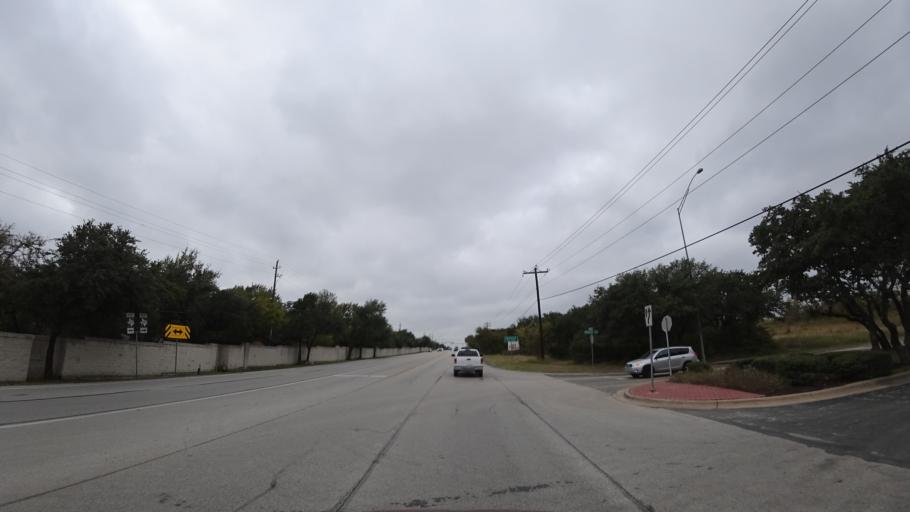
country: US
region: Texas
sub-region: Williamson County
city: Anderson Mill
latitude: 30.4648
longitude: -97.8078
